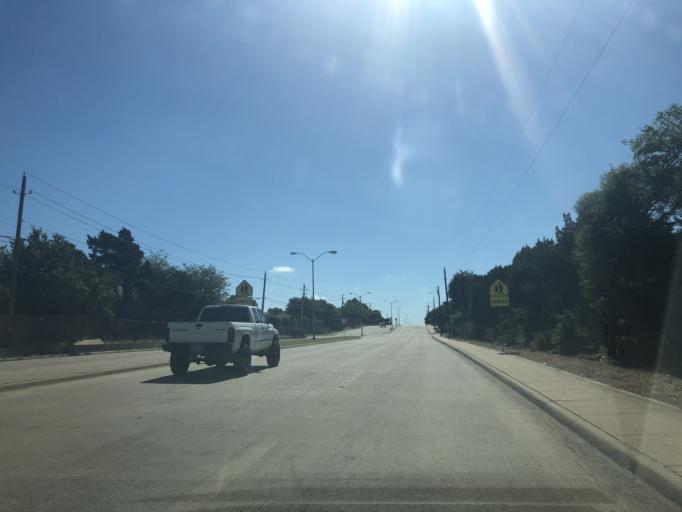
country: US
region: Texas
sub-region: Dallas County
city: Duncanville
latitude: 32.6623
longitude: -96.9344
